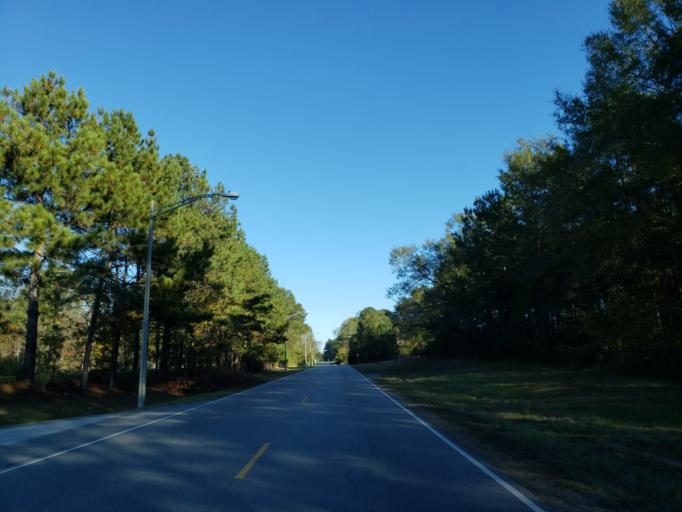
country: US
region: Mississippi
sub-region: Forrest County
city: Hattiesburg
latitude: 31.2665
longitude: -89.2792
